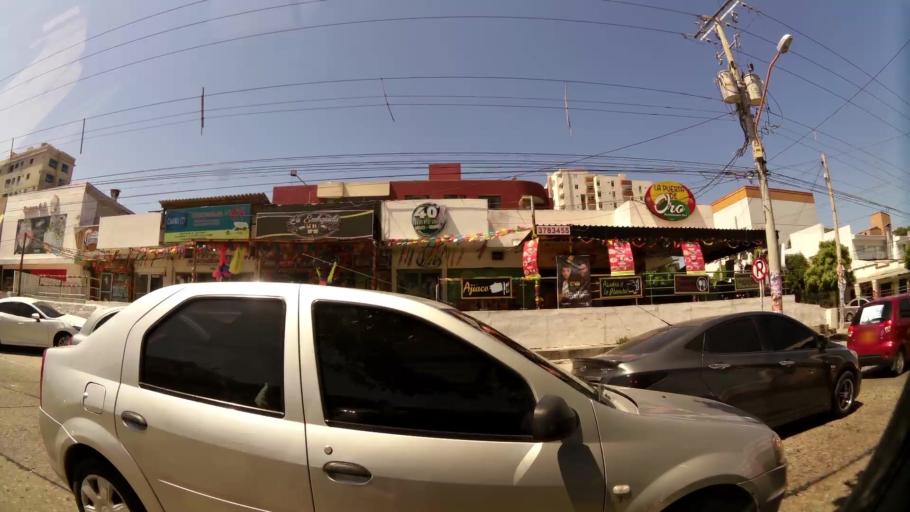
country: CO
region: Atlantico
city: Barranquilla
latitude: 11.0005
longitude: -74.8193
